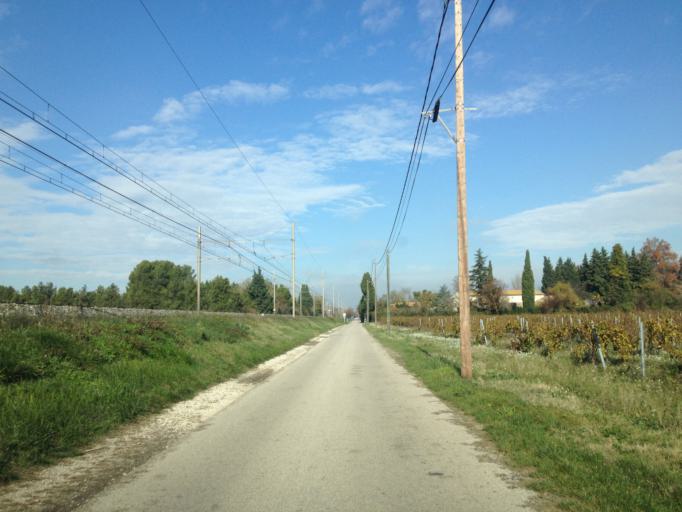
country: FR
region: Provence-Alpes-Cote d'Azur
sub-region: Departement du Vaucluse
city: Courthezon
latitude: 44.0770
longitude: 4.8905
